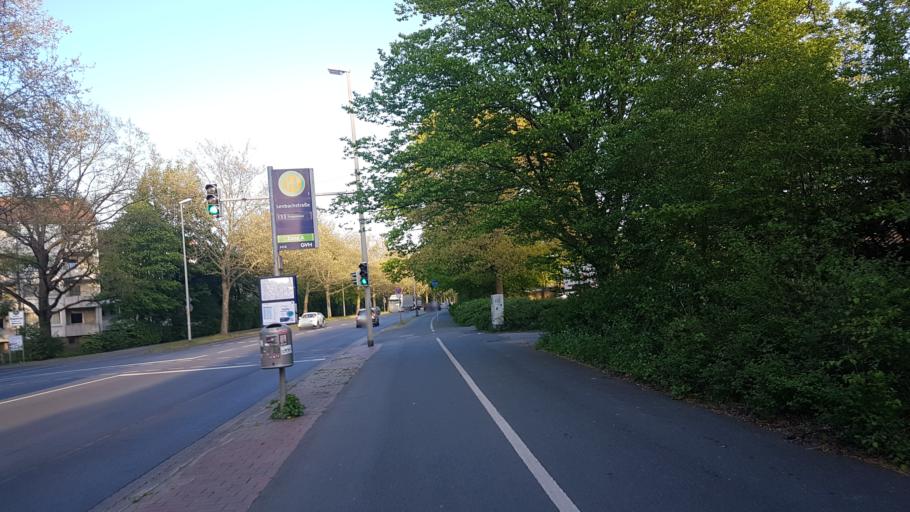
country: DE
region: Lower Saxony
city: Hannover
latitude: 52.3979
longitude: 9.7852
